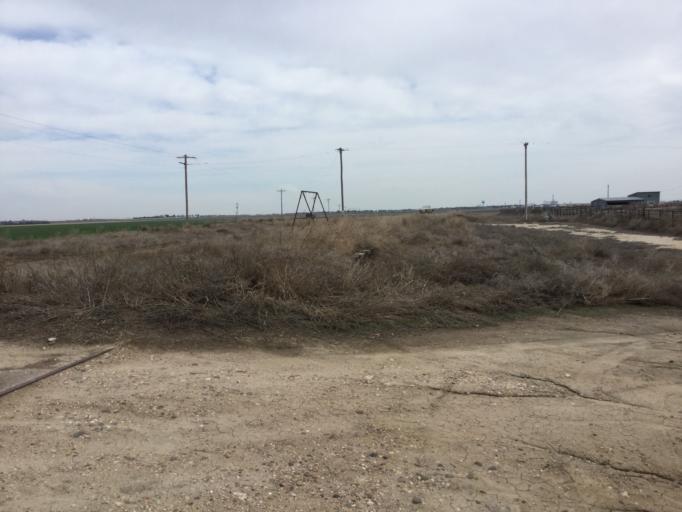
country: US
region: Kansas
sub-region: Scott County
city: Scott City
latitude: 38.4390
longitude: -100.9155
